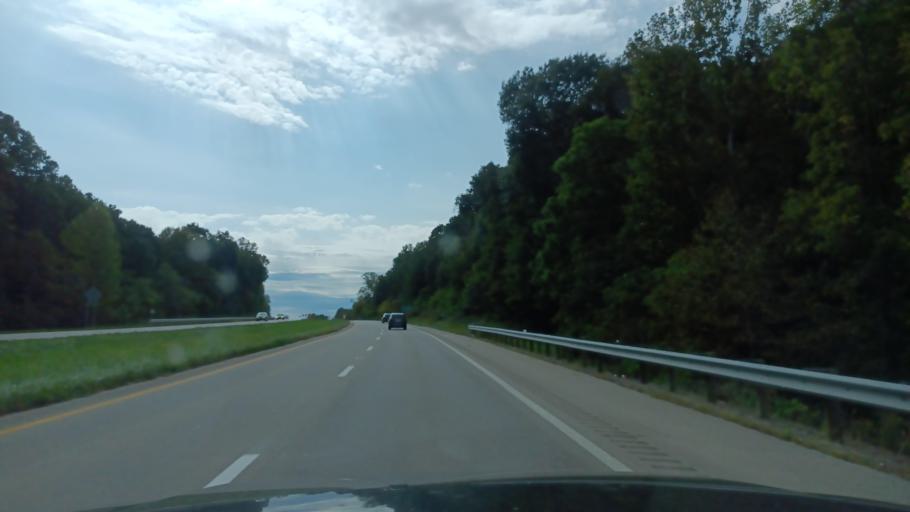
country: US
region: Ohio
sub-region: Athens County
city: Athens
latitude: 39.2856
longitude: -82.1470
